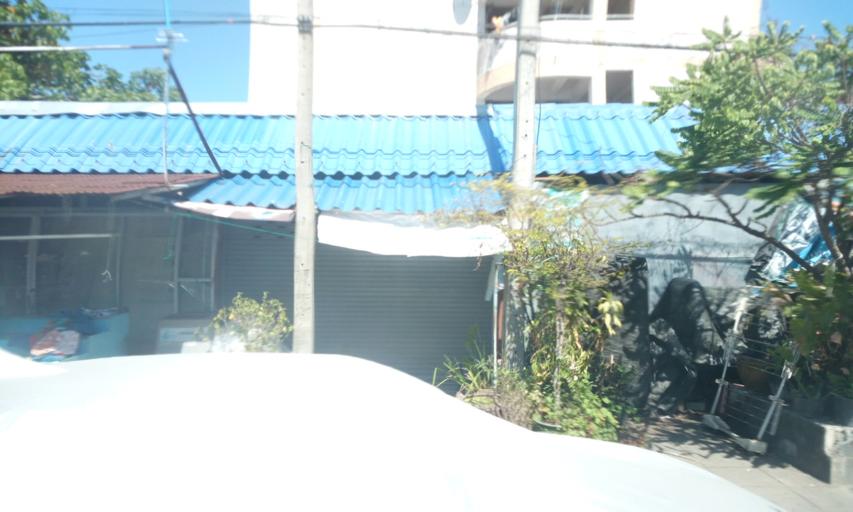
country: TH
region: Samut Prakan
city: Bang Bo District
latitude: 13.5585
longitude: 100.7652
